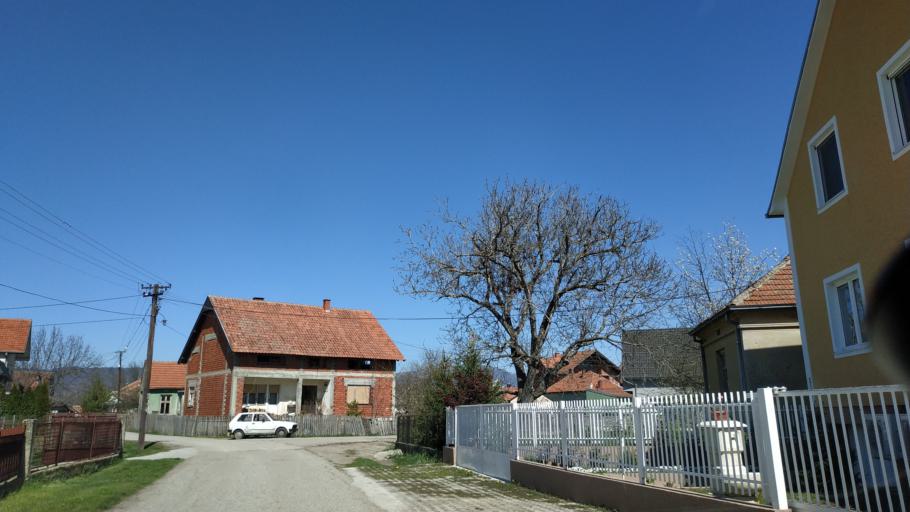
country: RS
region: Central Serbia
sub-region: Nisavski Okrug
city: Aleksinac
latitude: 43.5119
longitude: 21.6983
